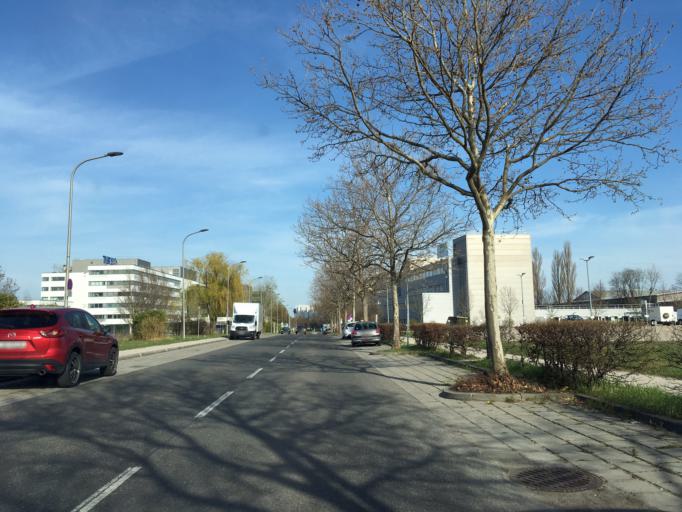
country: AT
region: Lower Austria
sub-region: Politischer Bezirk Modling
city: Brunn am Gebirge
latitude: 48.1142
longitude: 16.2908
